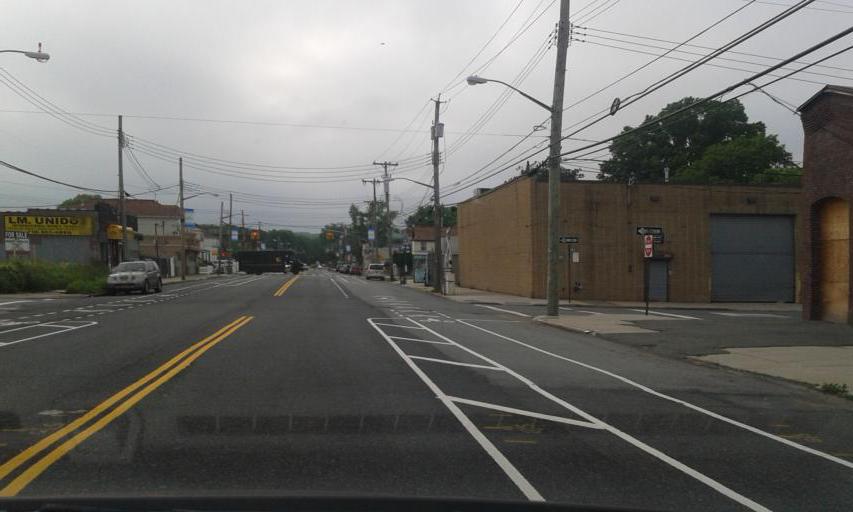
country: US
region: New York
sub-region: Richmond County
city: Staten Island
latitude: 40.5727
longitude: -74.0937
